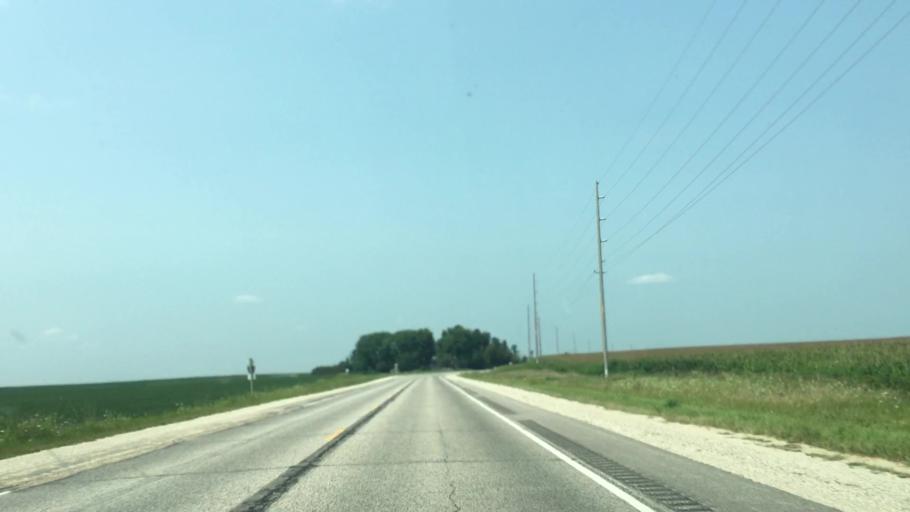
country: US
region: Iowa
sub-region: Fayette County
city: West Union
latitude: 42.9082
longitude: -91.8129
